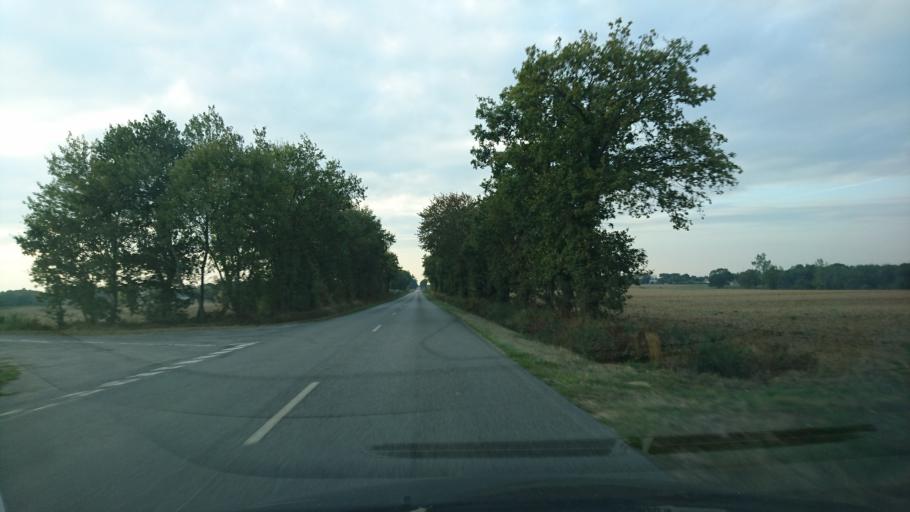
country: FR
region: Brittany
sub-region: Departement du Morbihan
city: Saint-Vincent-sur-Oust
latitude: 47.7038
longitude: -2.1539
